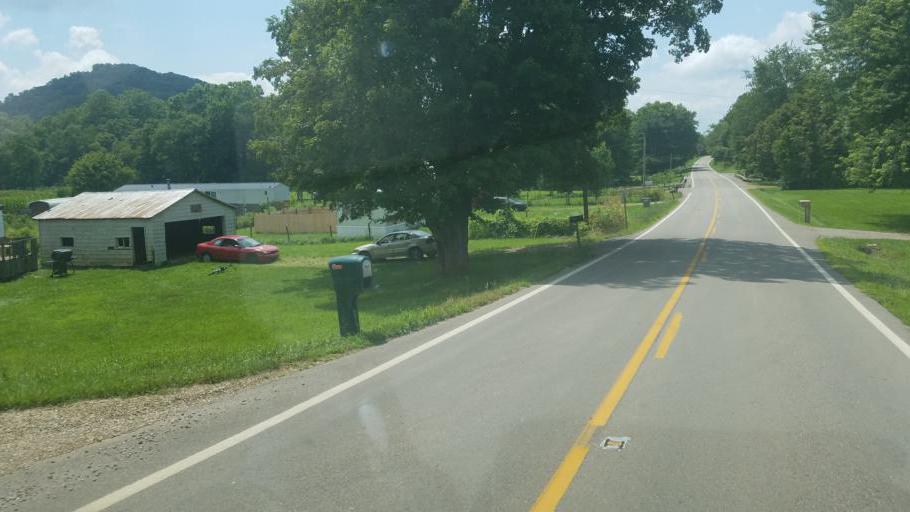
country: US
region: Ohio
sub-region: Ross County
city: Kingston
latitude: 39.3457
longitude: -82.7240
